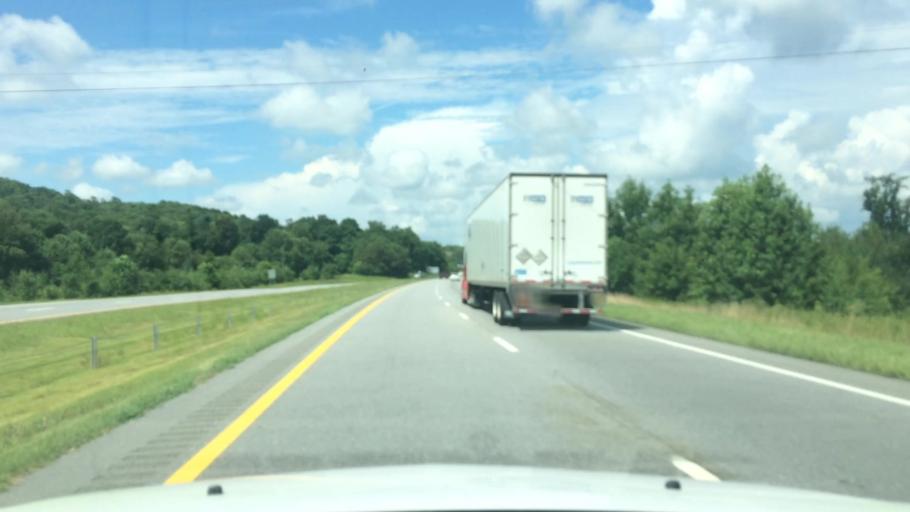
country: US
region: North Carolina
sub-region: Wilkes County
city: North Wilkesboro
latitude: 36.1514
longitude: -81.0016
